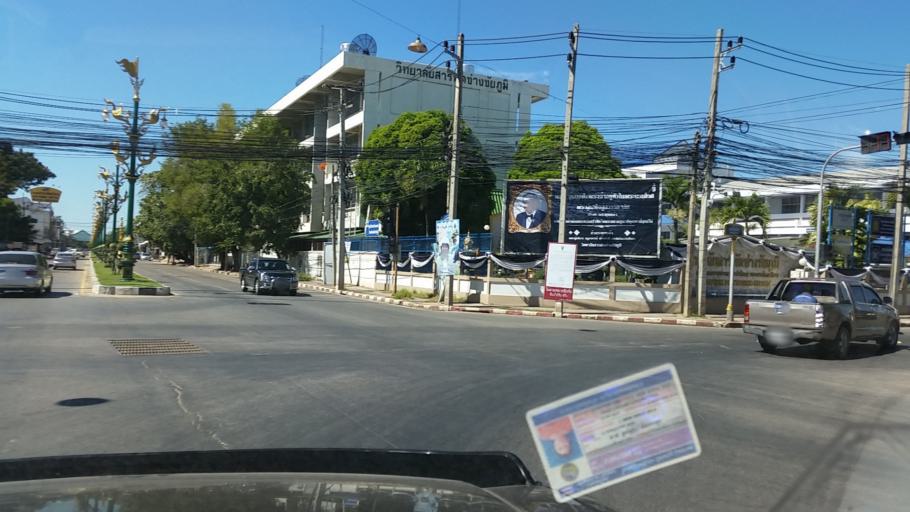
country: TH
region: Chaiyaphum
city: Chaiyaphum
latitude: 15.8071
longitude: 102.0289
